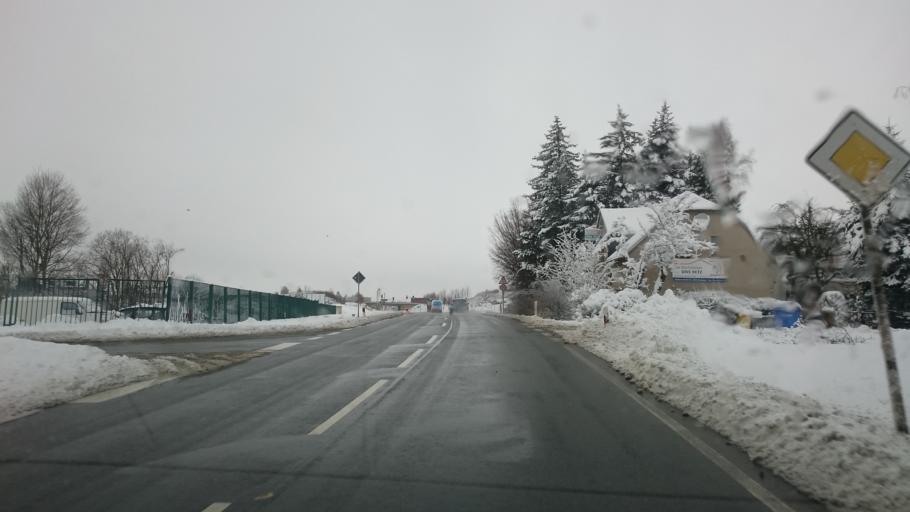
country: DE
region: Saxony
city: Reinsdorf
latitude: 50.6791
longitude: 12.5875
